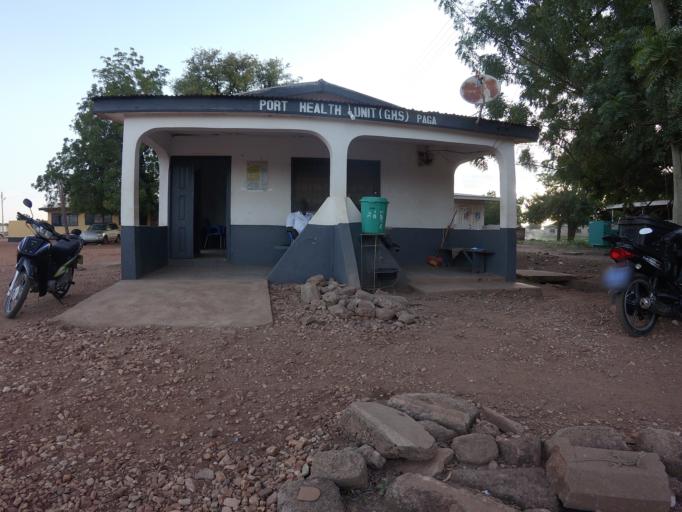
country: GH
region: Upper East
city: Navrongo
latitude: 10.9962
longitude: -1.1142
